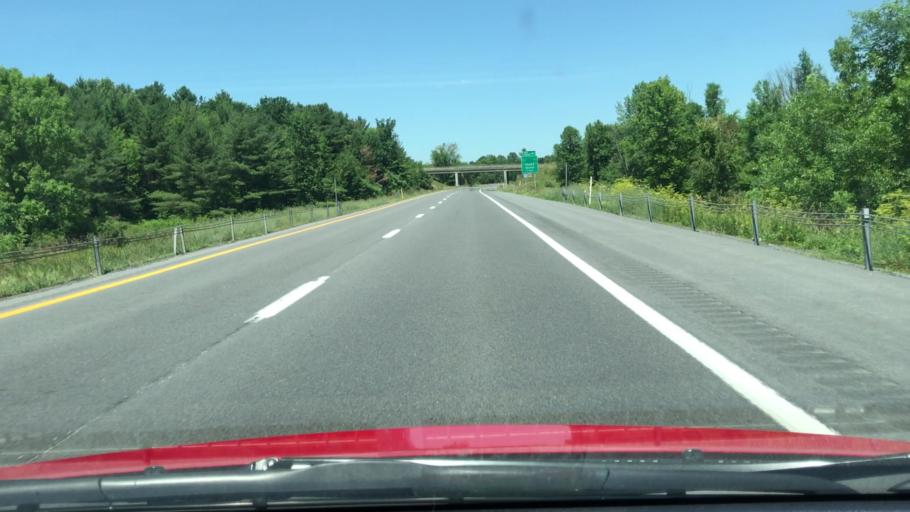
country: US
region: New York
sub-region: Clinton County
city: Champlain
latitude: 44.8681
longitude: -73.4505
